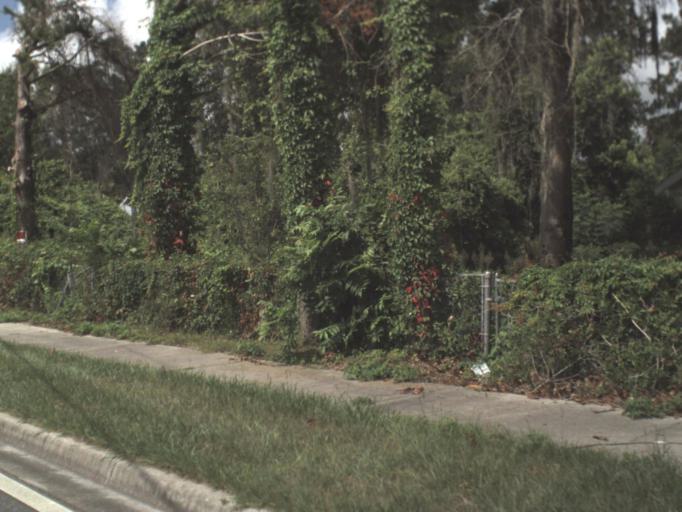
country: US
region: Florida
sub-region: Columbia County
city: Lake City
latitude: 30.1531
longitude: -82.6397
